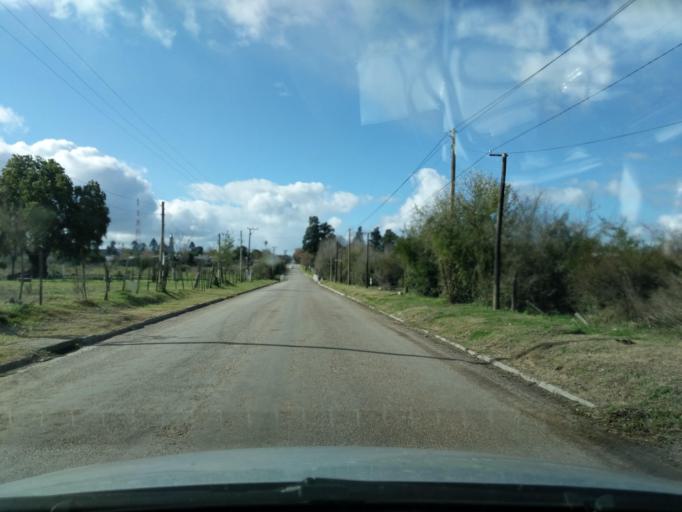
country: UY
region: Florida
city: Florida
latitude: -34.1088
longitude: -56.2199
